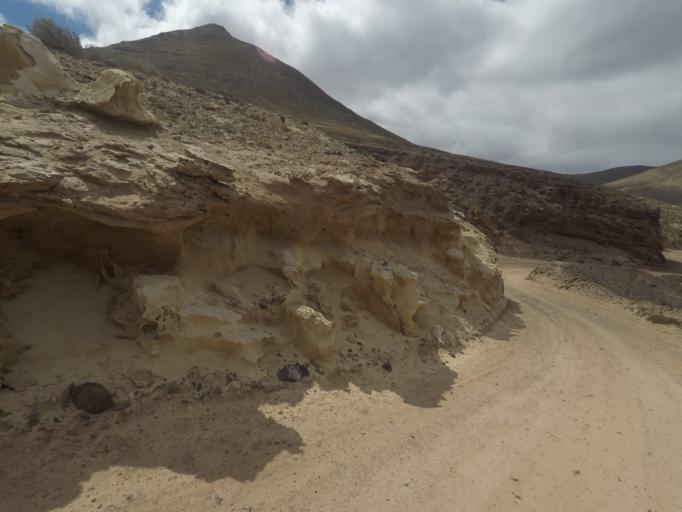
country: PT
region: Madeira
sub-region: Porto Santo
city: Vila de Porto Santo
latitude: 33.0652
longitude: -16.2966
